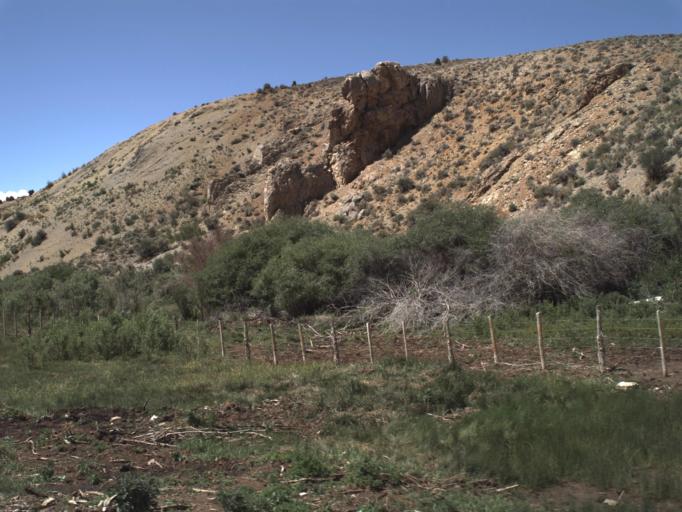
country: US
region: Utah
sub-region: Rich County
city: Randolph
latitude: 41.5017
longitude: -111.2816
